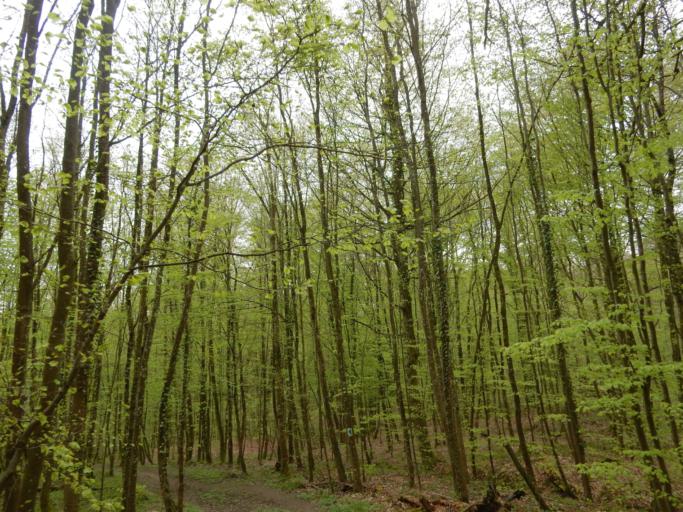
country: LU
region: Luxembourg
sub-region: Canton d'Esch-sur-Alzette
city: Petange
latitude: 49.5706
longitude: 5.8616
